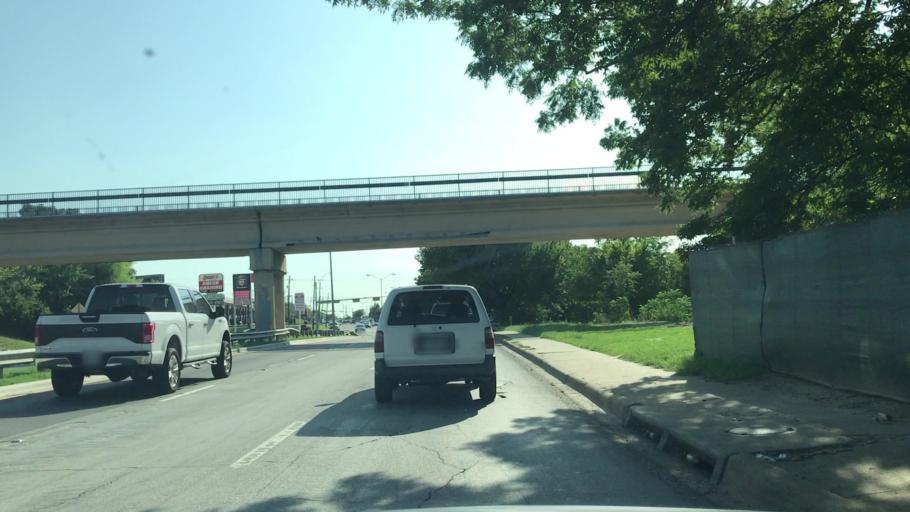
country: US
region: Texas
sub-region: Dallas County
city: Highland Park
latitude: 32.8636
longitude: -96.7474
